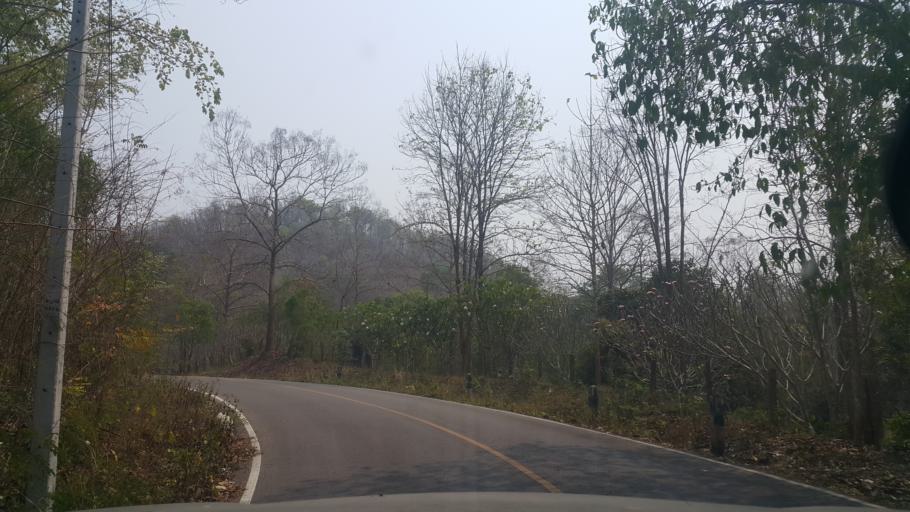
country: TH
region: Lampang
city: Sop Prap
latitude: 17.7657
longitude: 99.2360
